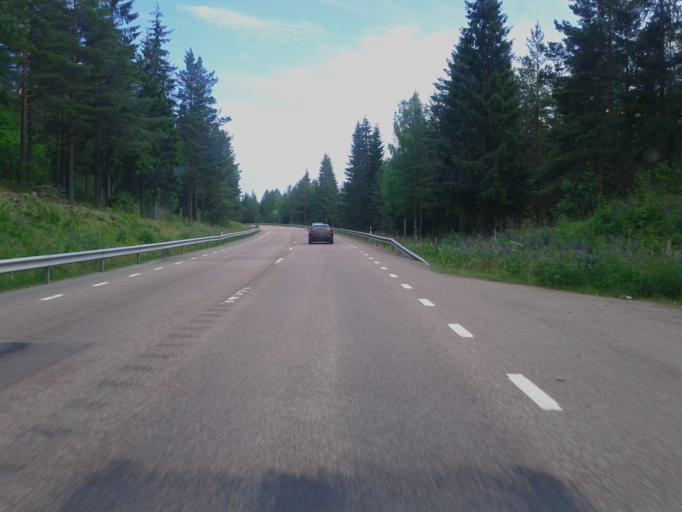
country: SE
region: Dalarna
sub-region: Faluns Kommun
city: Grycksbo
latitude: 60.7055
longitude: 15.4665
